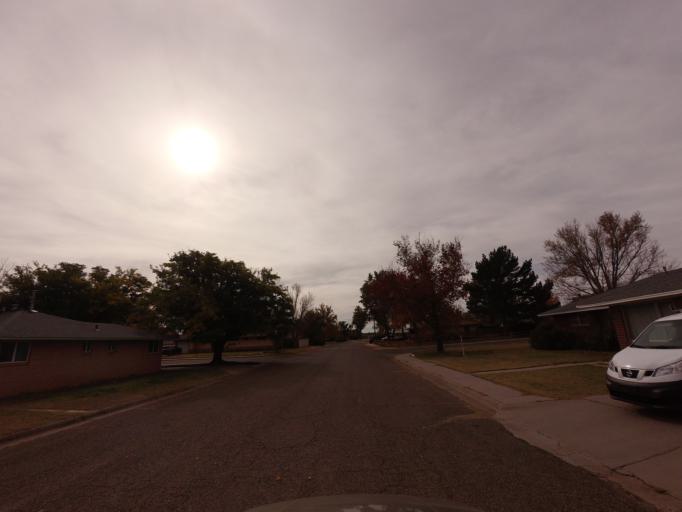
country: US
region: New Mexico
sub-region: Curry County
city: Clovis
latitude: 34.4242
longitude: -103.2095
